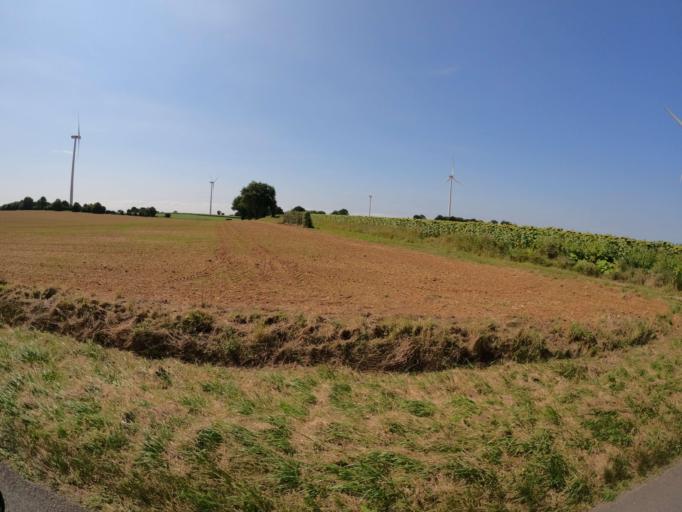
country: FR
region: Poitou-Charentes
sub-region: Departement des Deux-Sevres
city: Melle
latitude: 46.2384
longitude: -0.1753
